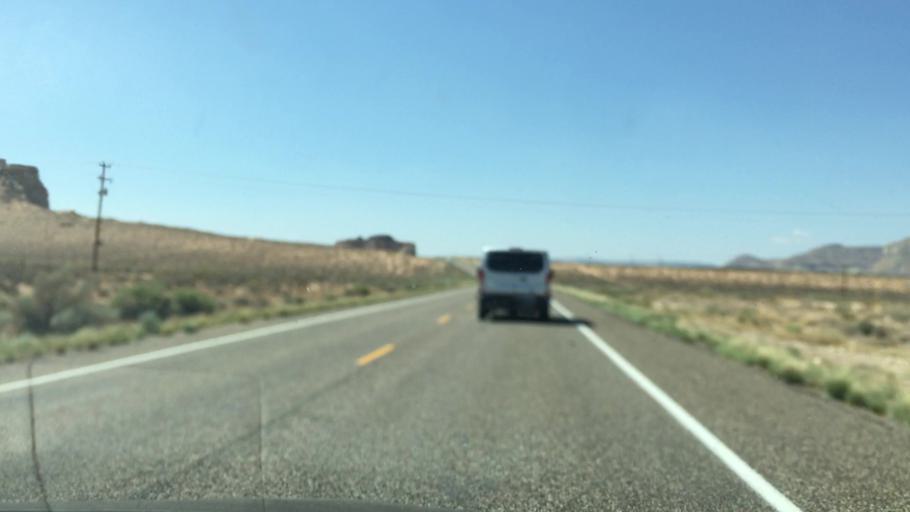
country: US
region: Arizona
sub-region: Coconino County
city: Page
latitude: 37.0269
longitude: -111.6008
